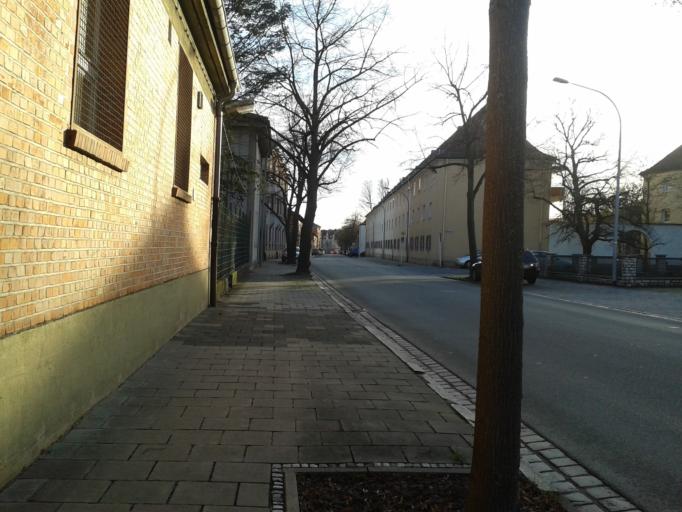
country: DE
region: Bavaria
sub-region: Upper Franconia
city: Bamberg
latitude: 49.9049
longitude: 10.9127
